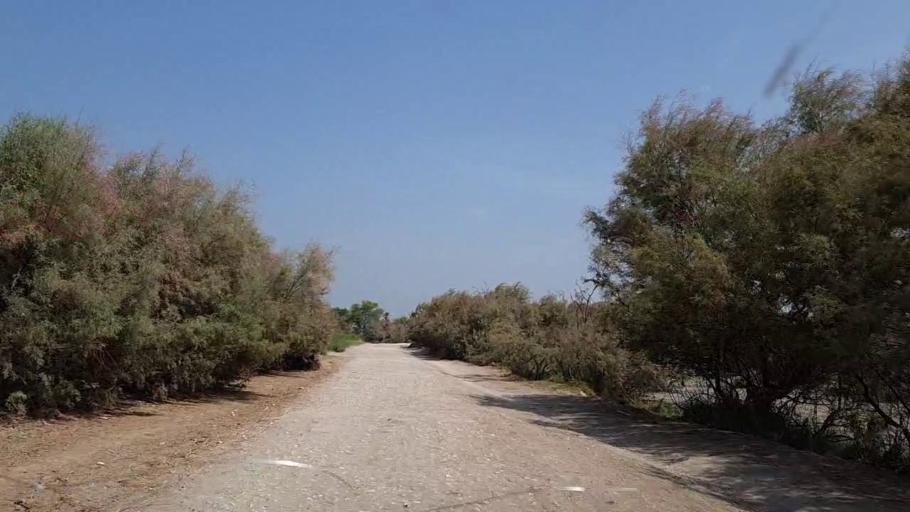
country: PK
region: Sindh
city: Adilpur
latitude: 27.8251
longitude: 69.3004
